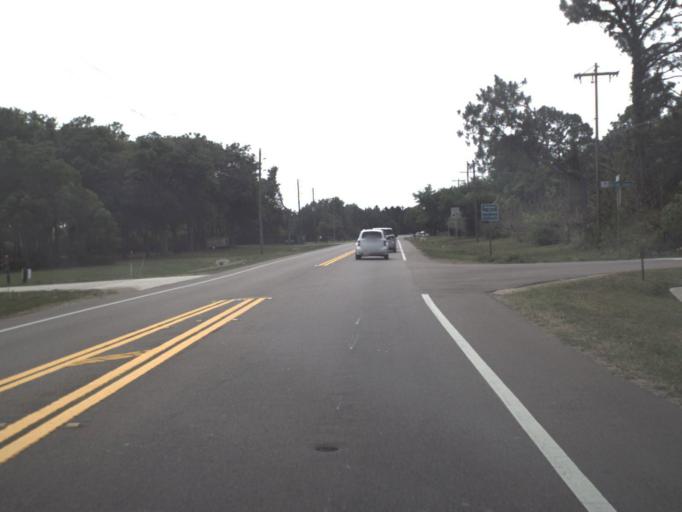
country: US
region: Florida
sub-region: Lake County
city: Mount Dora
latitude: 28.8451
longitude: -81.6338
